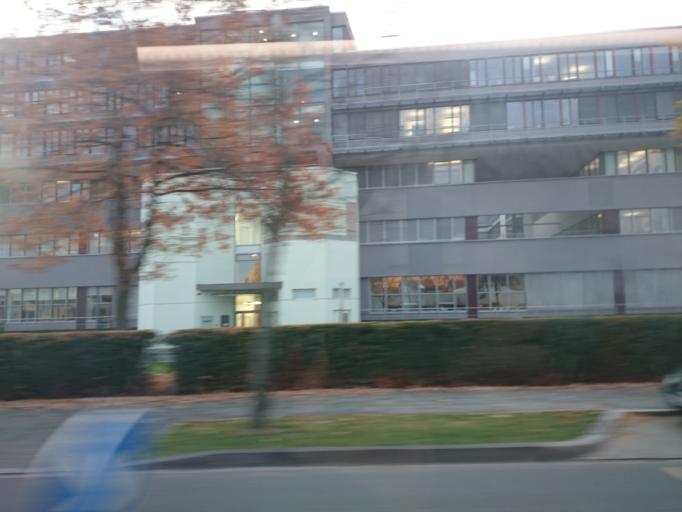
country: DE
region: Bavaria
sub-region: Regierungsbezirk Mittelfranken
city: Wendelstein
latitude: 49.4125
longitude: 11.1345
